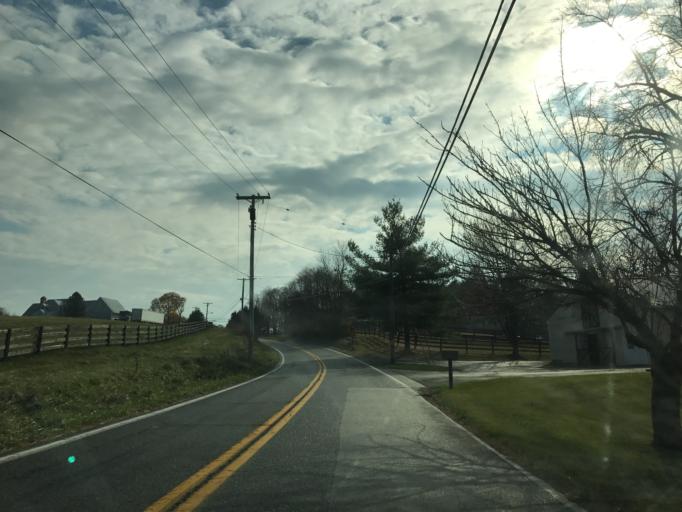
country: US
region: Maryland
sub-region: Baltimore County
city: Hunt Valley
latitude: 39.5689
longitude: -76.5938
